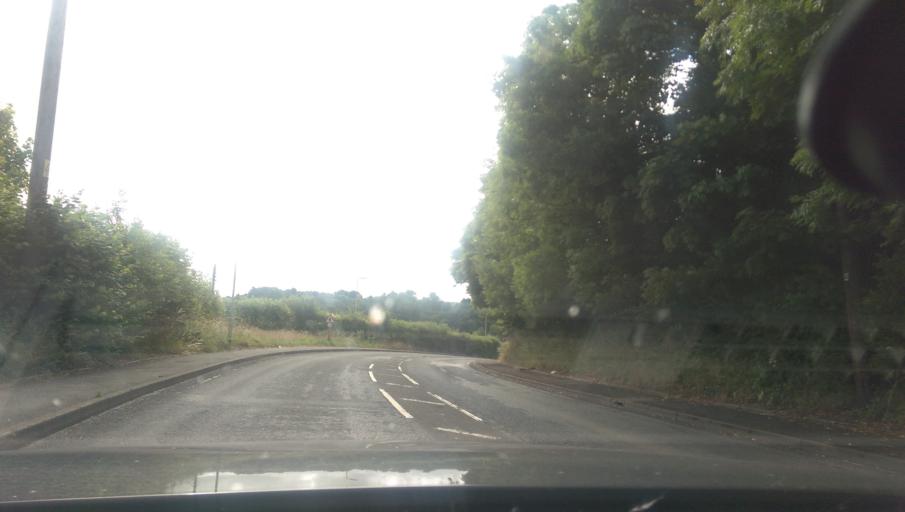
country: GB
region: England
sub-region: Devon
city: Okehampton
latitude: 50.7243
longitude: -3.9173
